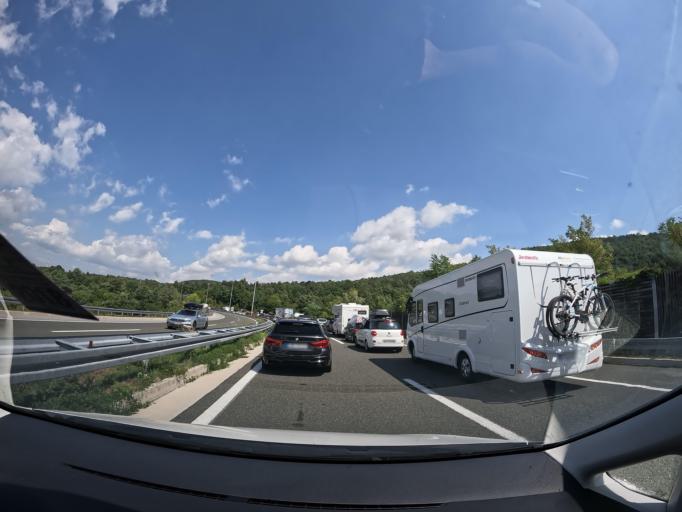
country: SI
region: Ilirska Bistrica
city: Ilirska Bistrica
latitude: 45.4862
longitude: 14.2836
